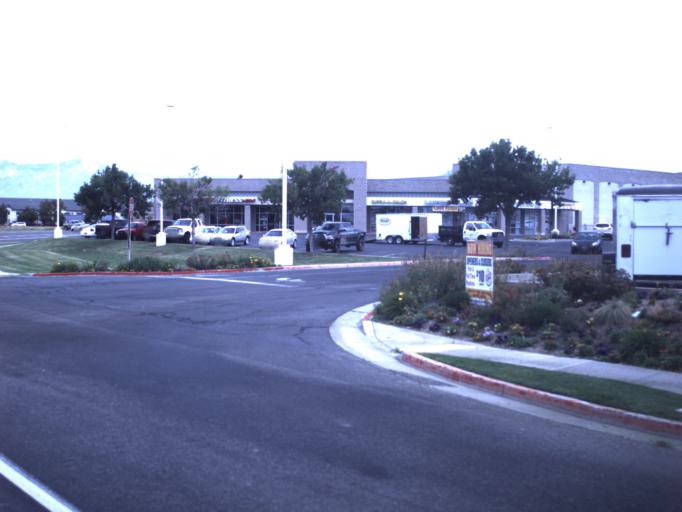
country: US
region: Utah
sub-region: Weber County
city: West Haven
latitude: 41.1765
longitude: -112.0644
